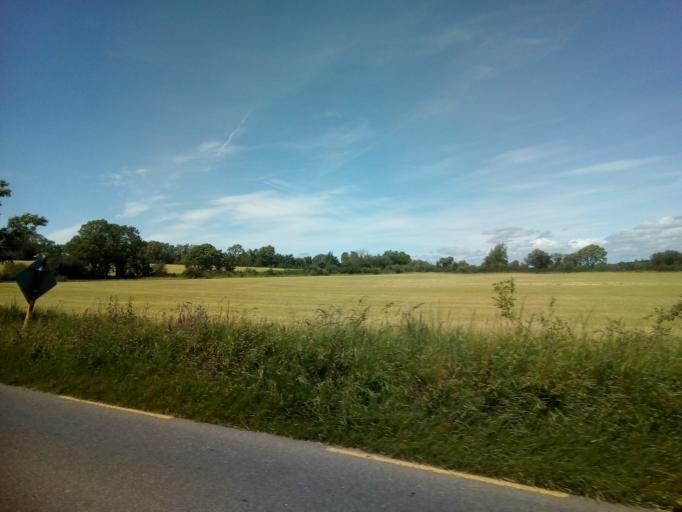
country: IE
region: Leinster
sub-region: Loch Garman
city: New Ross
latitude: 52.2656
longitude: -6.7806
